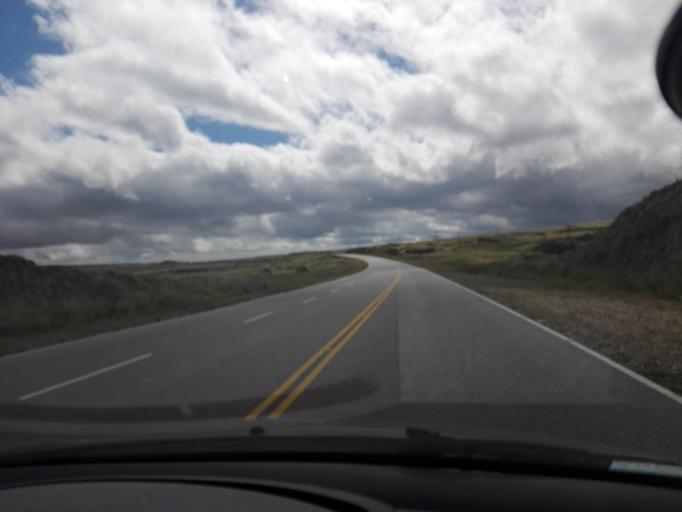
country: AR
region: Cordoba
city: Mina Clavero
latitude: -31.6101
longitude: -64.8317
